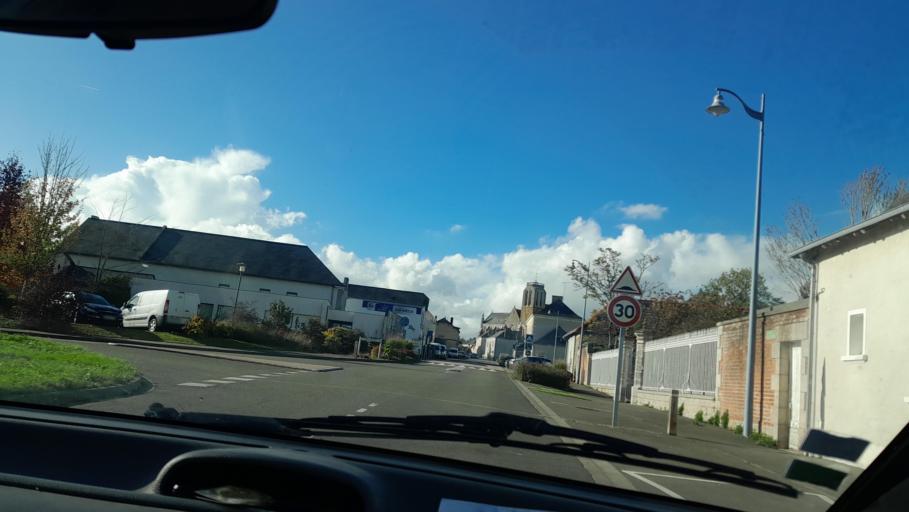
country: FR
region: Pays de la Loire
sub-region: Departement de la Mayenne
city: Cosse-le-Vivien
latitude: 47.9596
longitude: -0.9770
